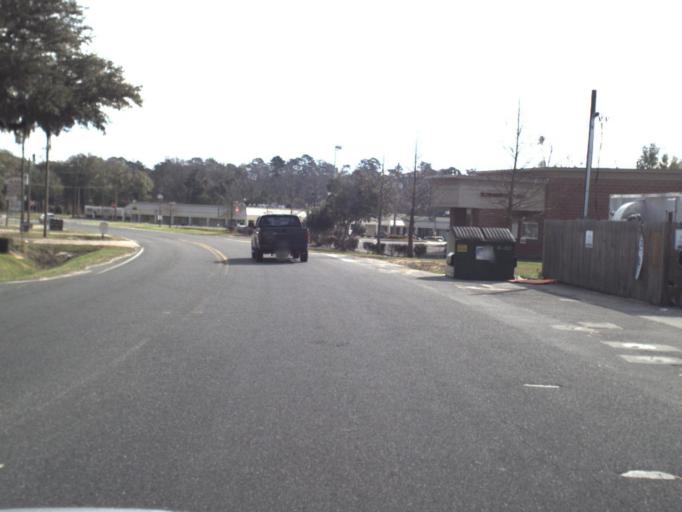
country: US
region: Florida
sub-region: Jackson County
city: Marianna
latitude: 30.7694
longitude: -85.2048
